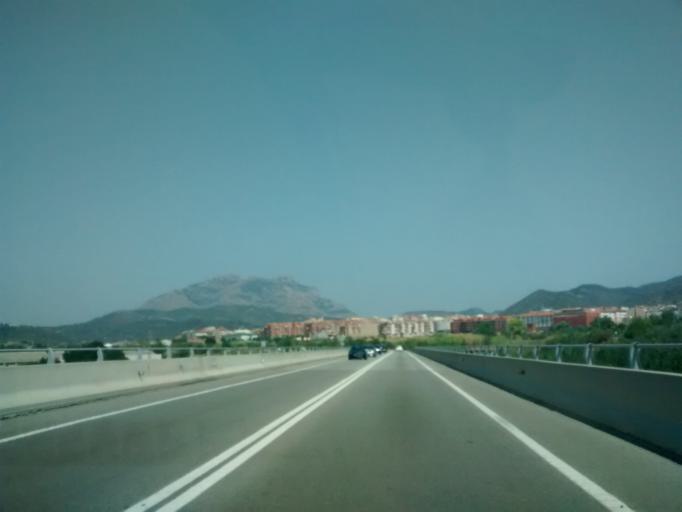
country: ES
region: Catalonia
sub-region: Provincia de Barcelona
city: Olesa de Montserrat
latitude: 41.5339
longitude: 1.9001
